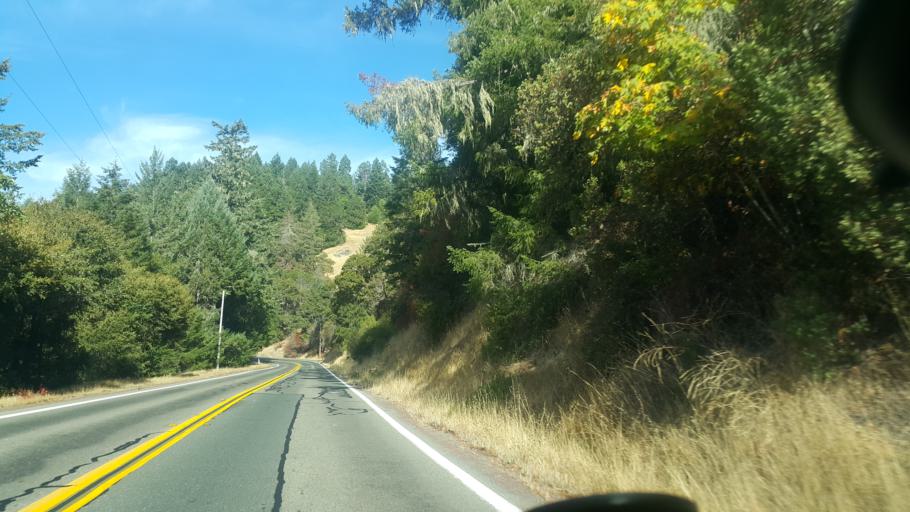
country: US
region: California
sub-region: Mendocino County
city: Brooktrails
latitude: 39.3880
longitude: -123.4298
